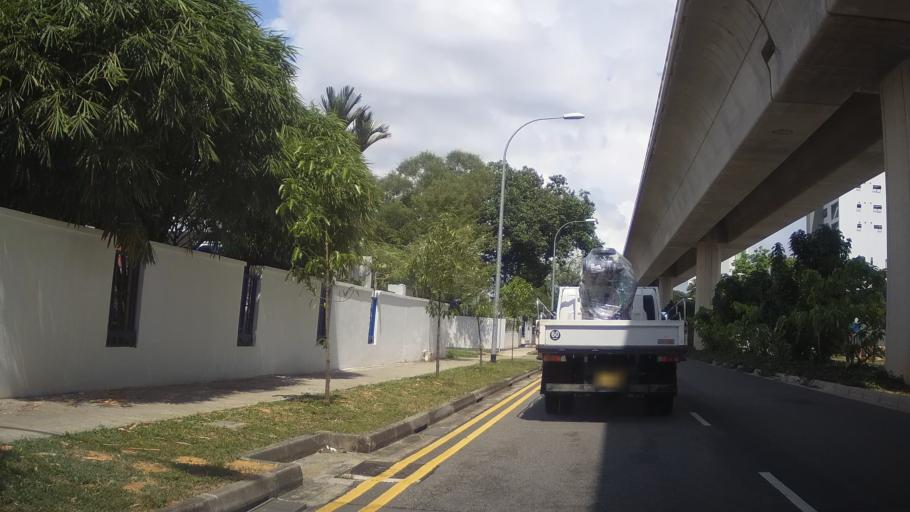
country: MY
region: Johor
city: Johor Bahru
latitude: 1.3275
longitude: 103.6732
